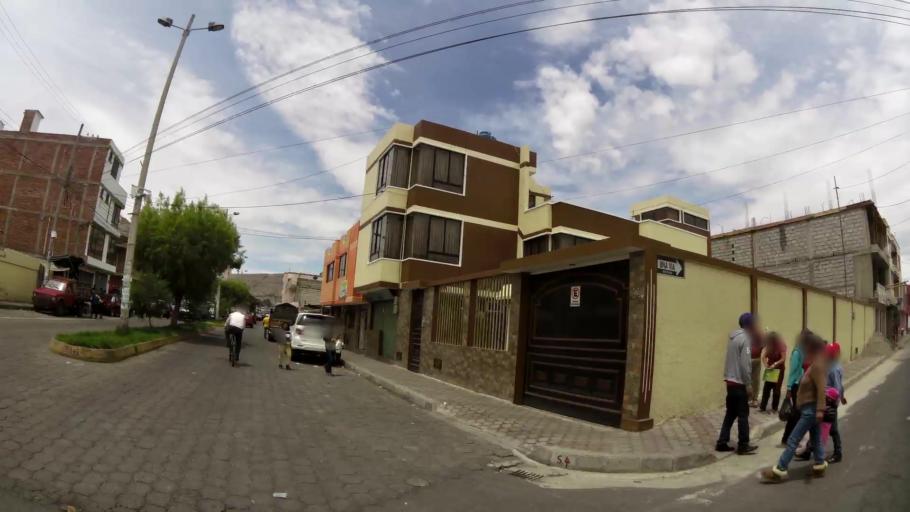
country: EC
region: Cotopaxi
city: San Miguel de Salcedo
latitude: -1.0456
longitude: -78.5917
